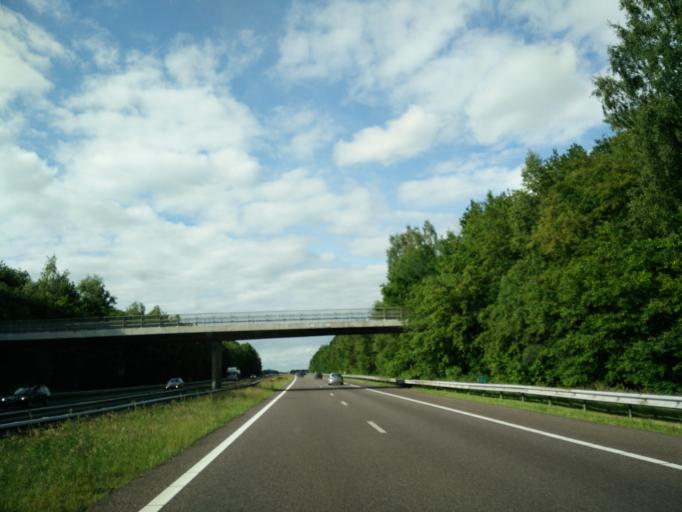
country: NL
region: Drenthe
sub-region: Gemeente Assen
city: Assen
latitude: 52.9244
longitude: 6.5342
